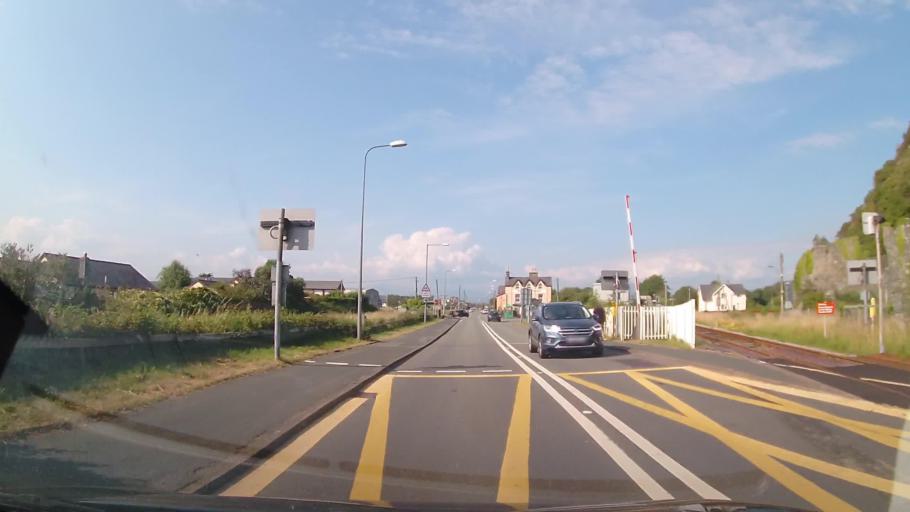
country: GB
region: Wales
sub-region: Gwynedd
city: Llanfair
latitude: 52.8601
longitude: -4.1109
